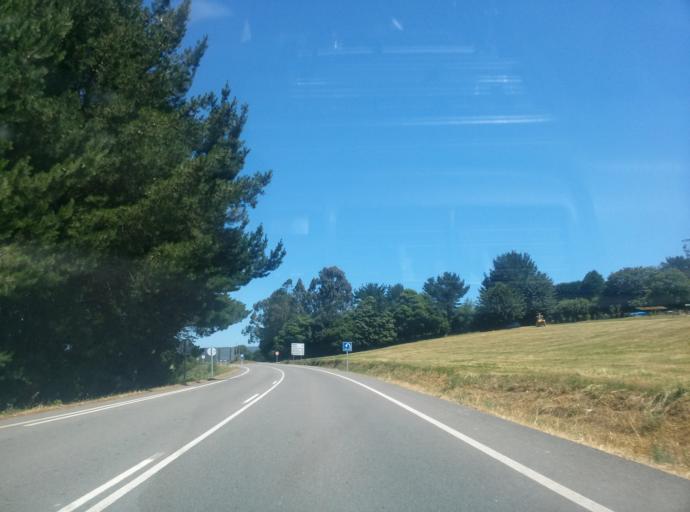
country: ES
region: Galicia
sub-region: Provincia de Lugo
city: Meira
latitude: 43.2306
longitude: -7.3442
